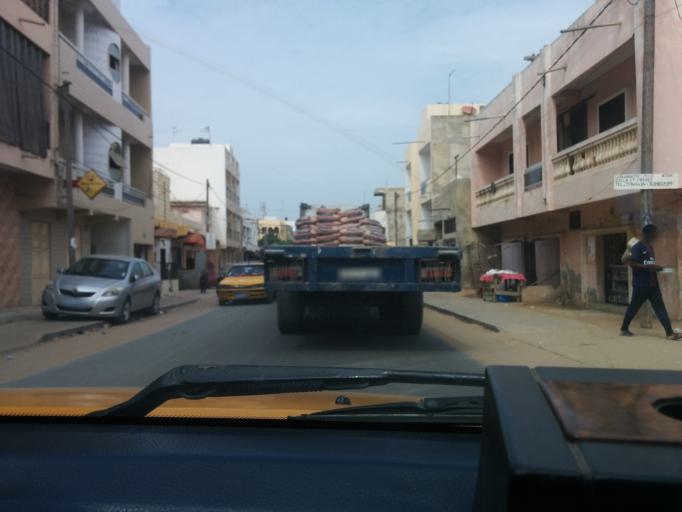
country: SN
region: Dakar
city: Grand Dakar
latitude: 14.7528
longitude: -17.4527
